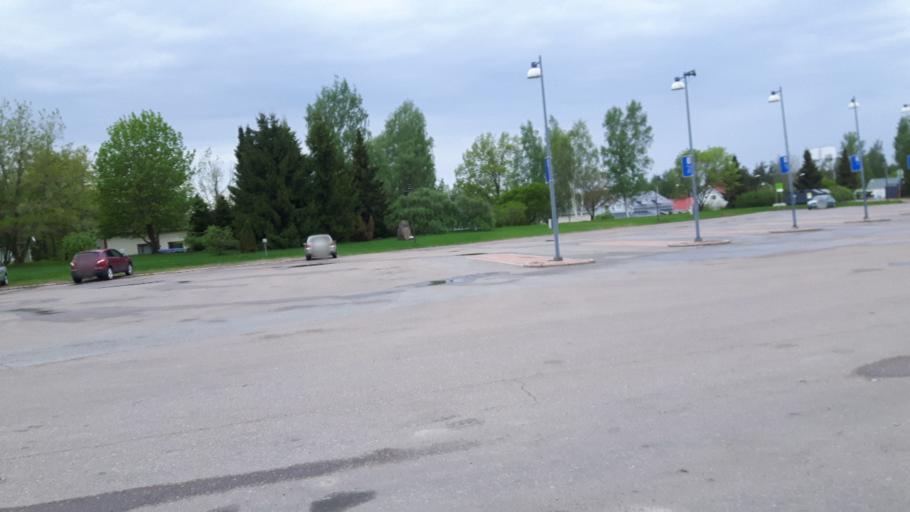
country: FI
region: Kymenlaakso
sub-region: Kotka-Hamina
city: Hamina
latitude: 60.5689
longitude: 27.1878
